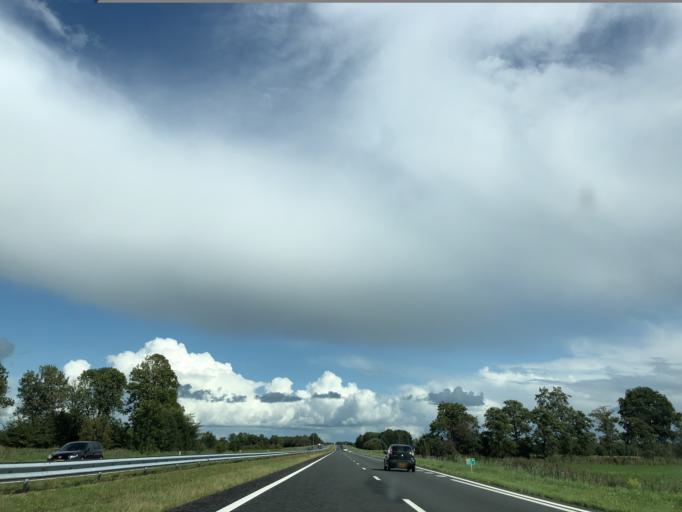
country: NL
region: Friesland
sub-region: Gemeente Smallingerland
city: Oudega
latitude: 53.1450
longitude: 6.0102
